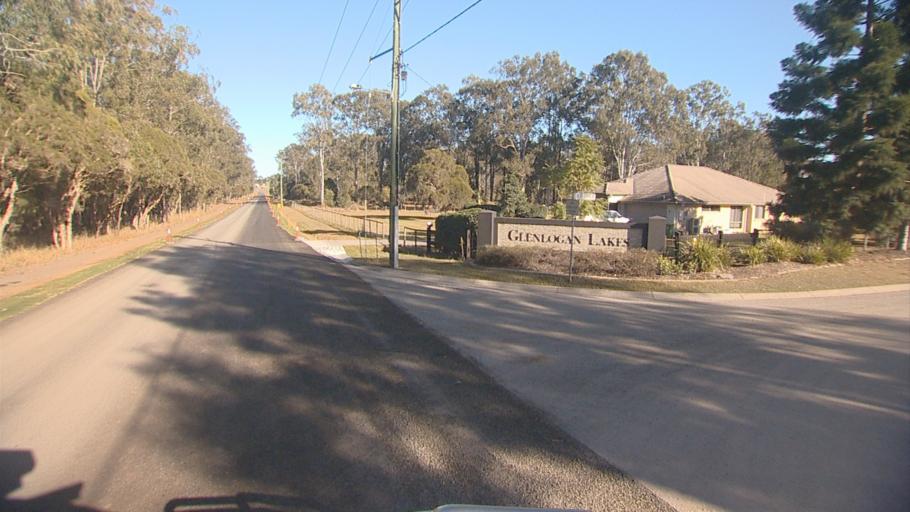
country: AU
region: Queensland
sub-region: Logan
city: Cedar Vale
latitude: -27.8334
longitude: 153.0008
